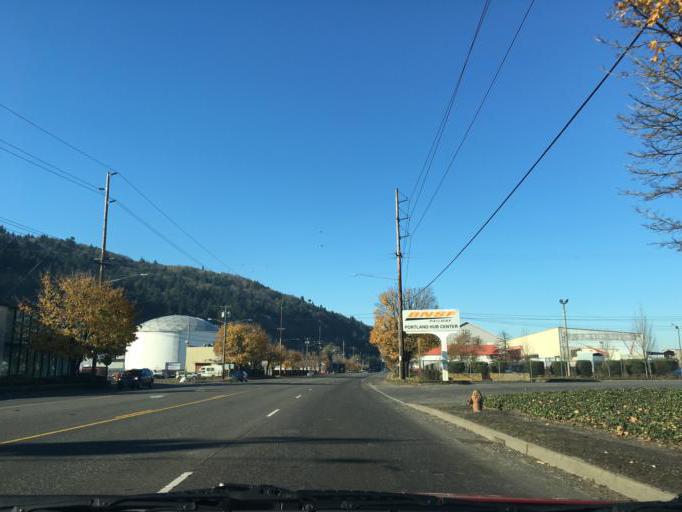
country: US
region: Oregon
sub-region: Multnomah County
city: Portland
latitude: 45.5511
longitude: -122.7234
